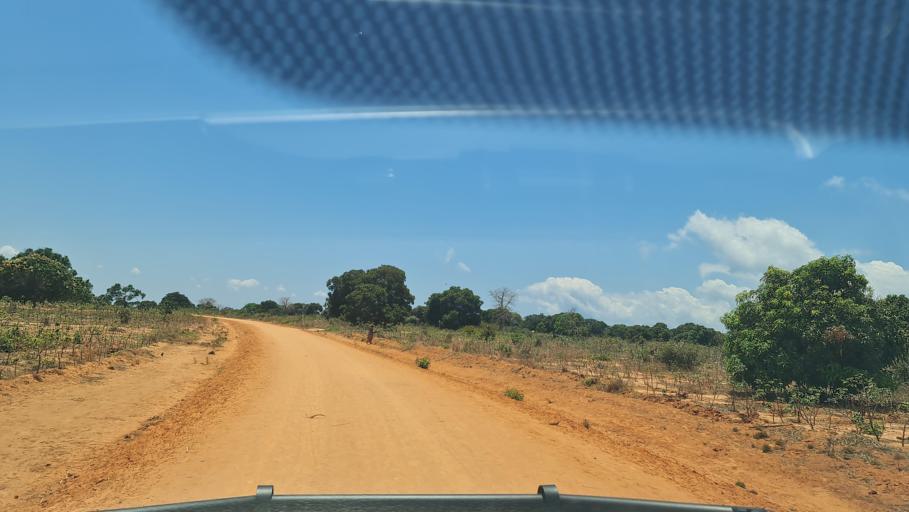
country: MZ
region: Nampula
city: Nacala
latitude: -14.2187
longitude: 40.6844
